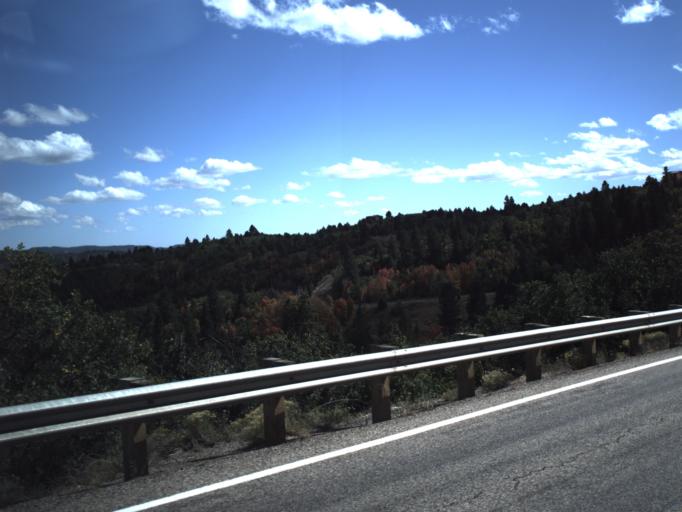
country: US
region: Utah
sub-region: Garfield County
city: Panguitch
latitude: 37.4936
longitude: -112.5302
